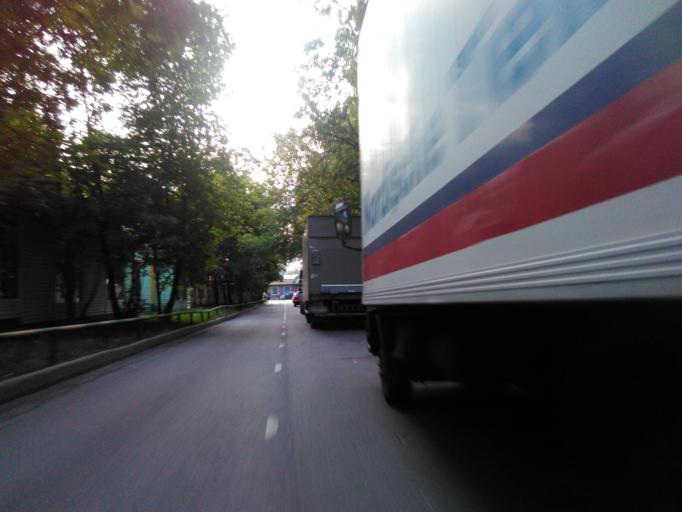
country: RU
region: Moscow
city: Yaroslavskiy
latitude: 55.8796
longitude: 37.7143
